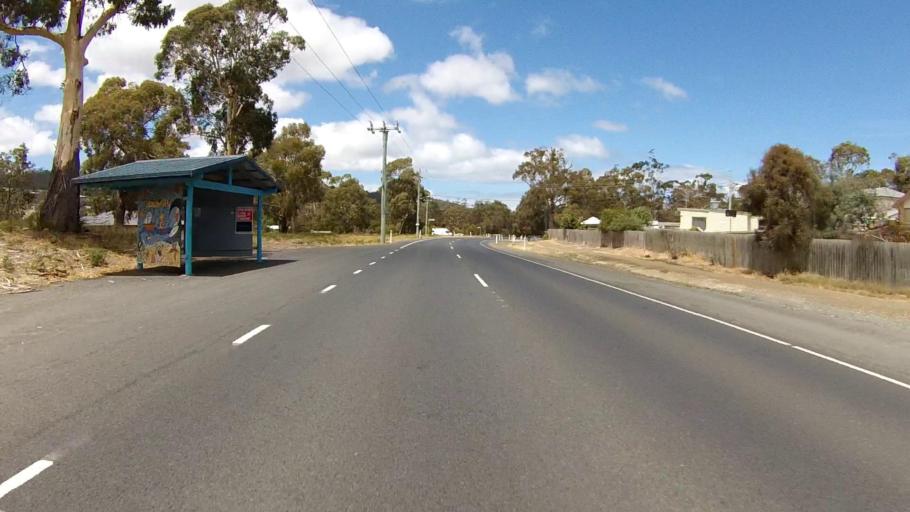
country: AU
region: Tasmania
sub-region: Sorell
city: Sorell
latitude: -42.8436
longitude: 147.6250
